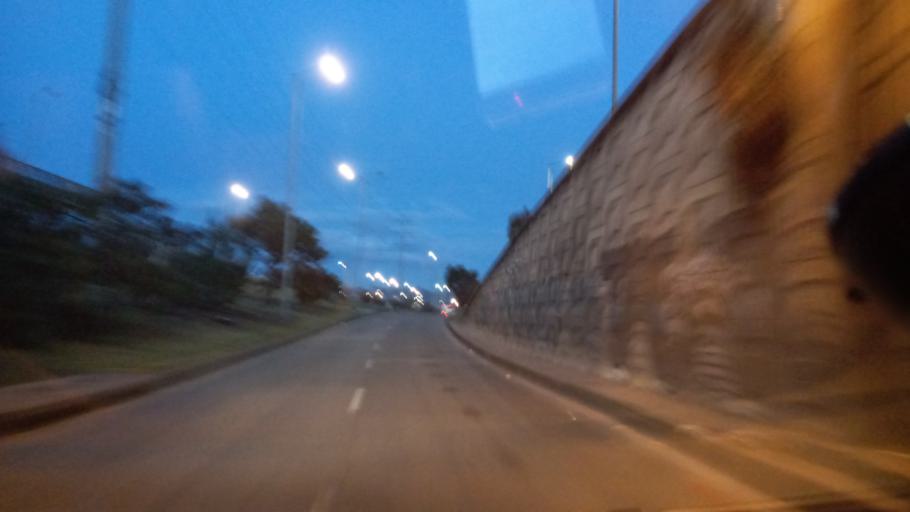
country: CO
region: Cundinamarca
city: Soacha
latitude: 4.5961
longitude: -74.1711
